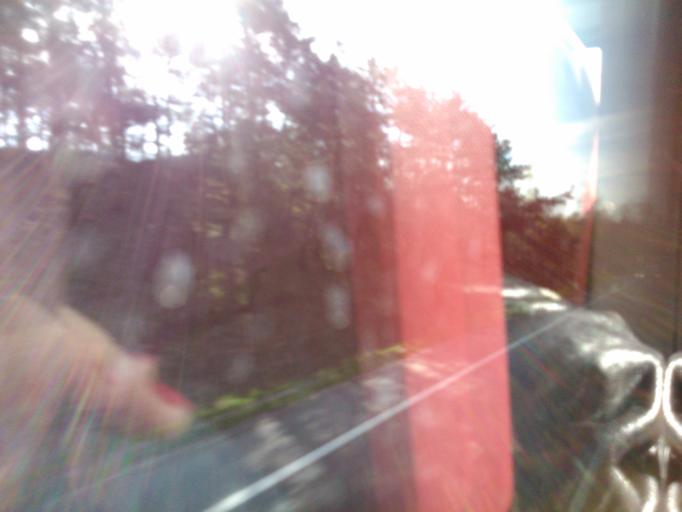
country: PL
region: Kujawsko-Pomorskie
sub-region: Powiat aleksandrowski
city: Aleksandrow Kujawski
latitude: 52.9439
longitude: 18.6974
